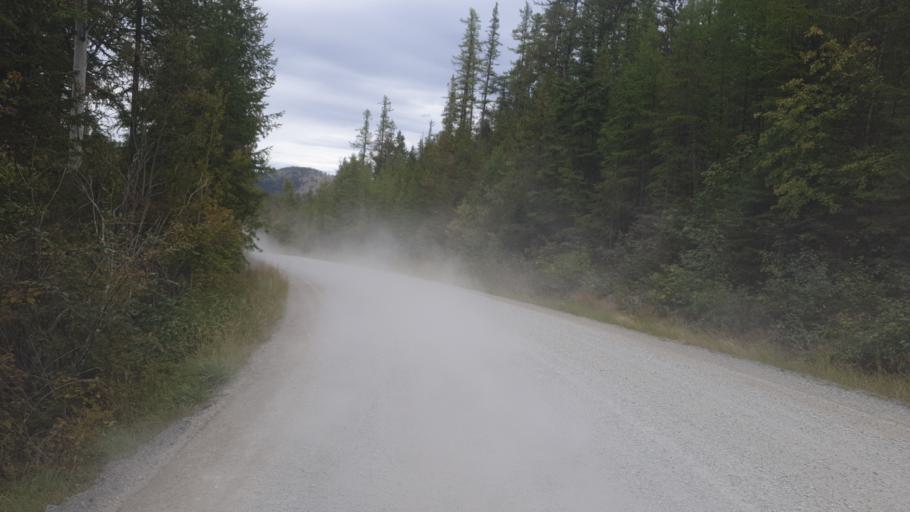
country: US
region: Montana
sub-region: Flathead County
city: Lakeside
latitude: 47.9926
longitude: -114.3244
